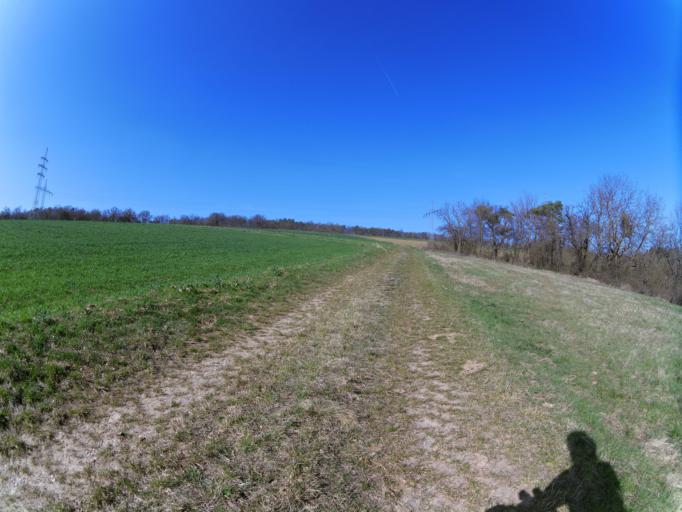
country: DE
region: Bavaria
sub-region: Regierungsbezirk Unterfranken
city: Greussenheim
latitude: 49.8043
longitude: 9.7602
